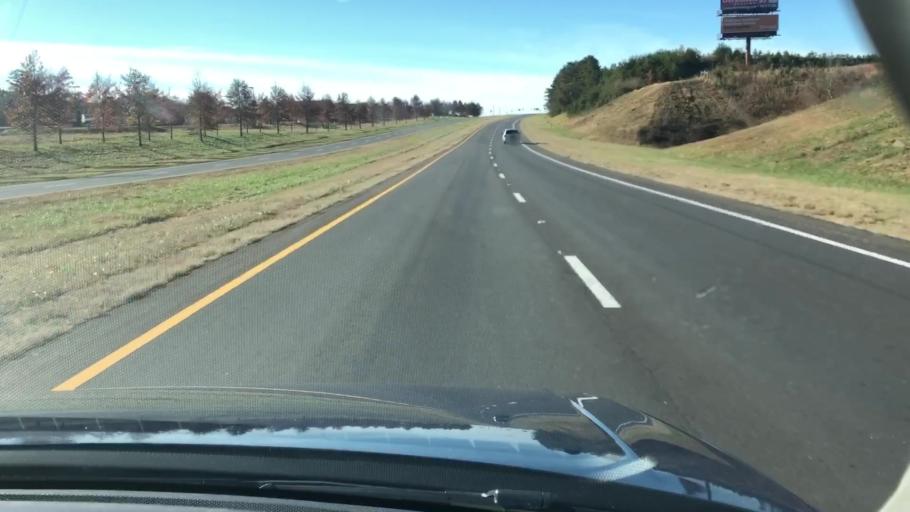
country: US
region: Georgia
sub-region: Gilmer County
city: Ellijay
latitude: 34.6625
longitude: -84.4892
